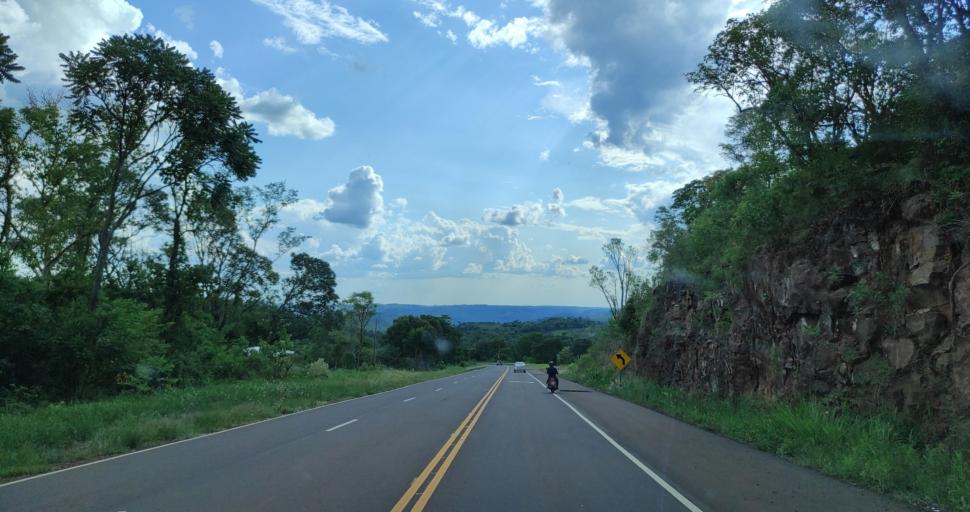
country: AR
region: Misiones
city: Bernardo de Irigoyen
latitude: -26.3042
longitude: -53.8163
